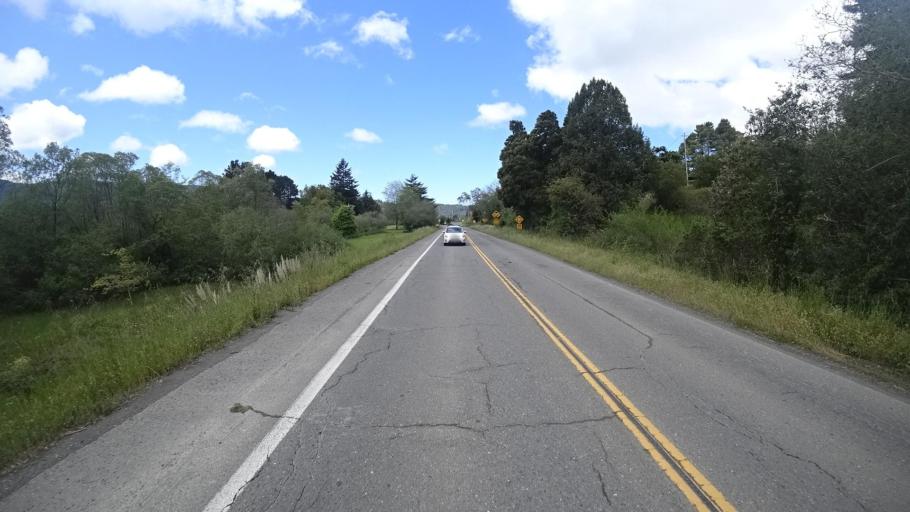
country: US
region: California
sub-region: Humboldt County
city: Blue Lake
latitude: 40.8861
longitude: -123.9932
